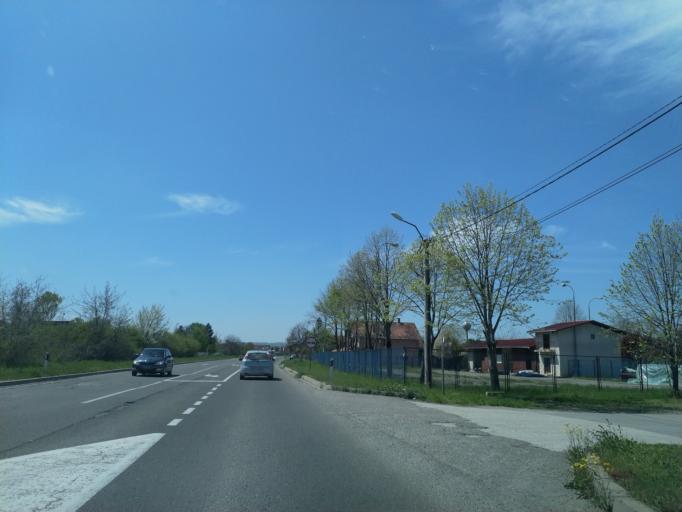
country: RS
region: Central Serbia
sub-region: Kolubarski Okrug
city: Lajkovac
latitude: 44.3699
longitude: 20.1780
